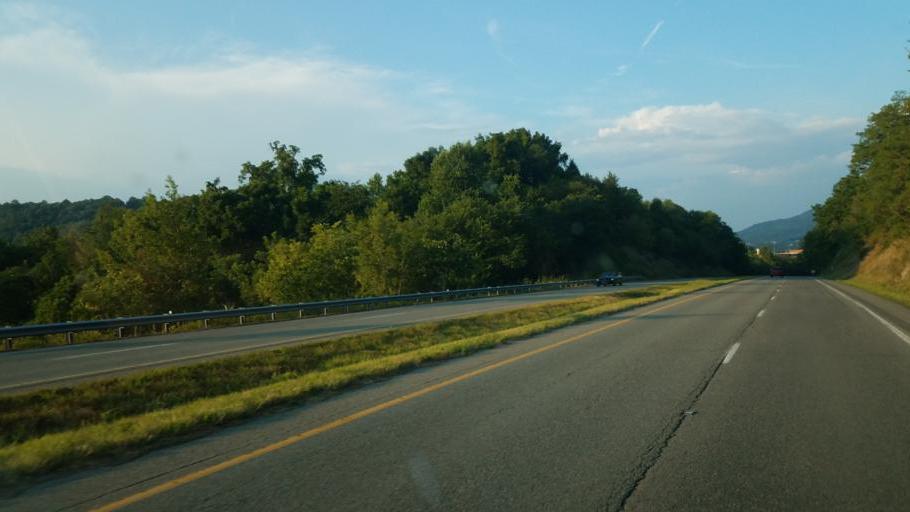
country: US
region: Virginia
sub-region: Scott County
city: Gate City
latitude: 36.6342
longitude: -82.5793
